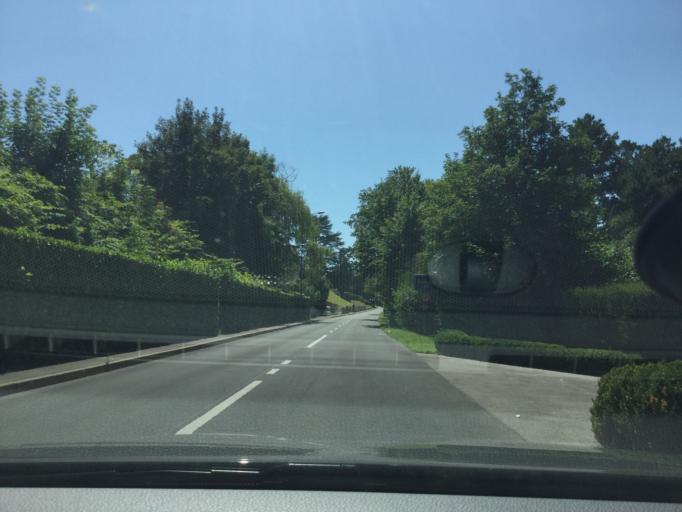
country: CH
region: Geneva
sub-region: Geneva
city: Anieres
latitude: 46.2828
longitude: 6.2289
